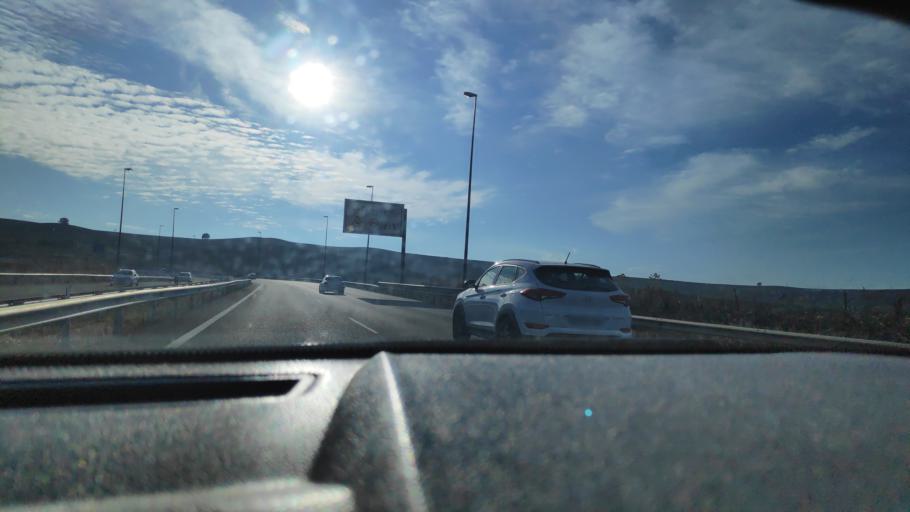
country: ES
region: Andalusia
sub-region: Province of Cordoba
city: La Victoria
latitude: 37.7748
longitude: -4.8227
